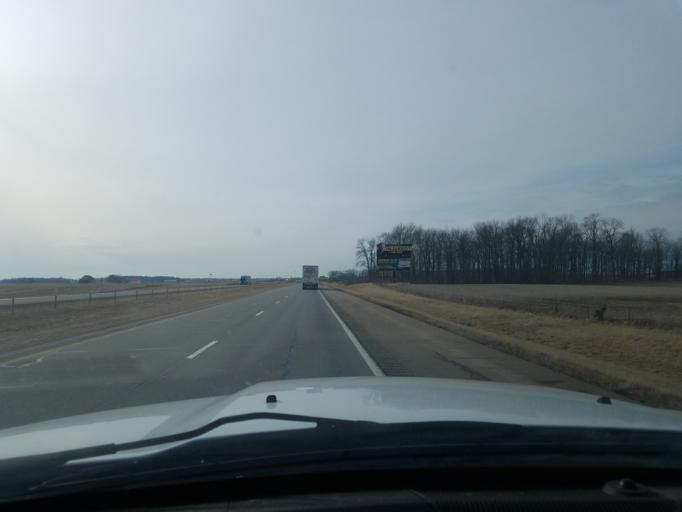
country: US
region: Indiana
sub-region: Henry County
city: New Castle
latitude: 39.8530
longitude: -85.3728
